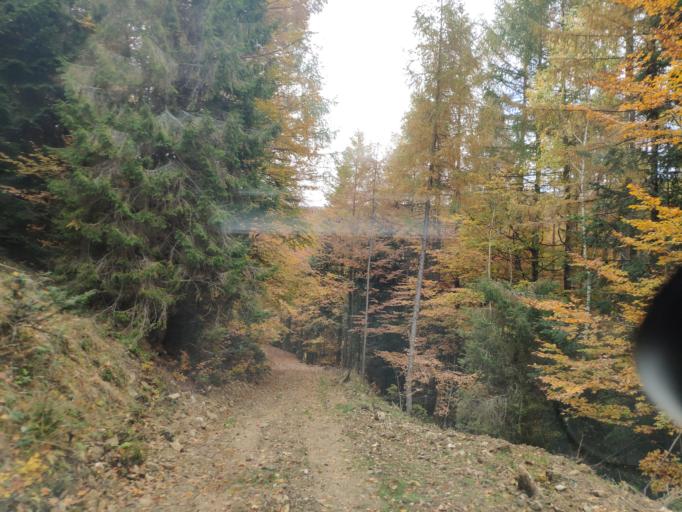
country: SK
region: Kosicky
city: Medzev
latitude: 48.7593
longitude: 20.9762
